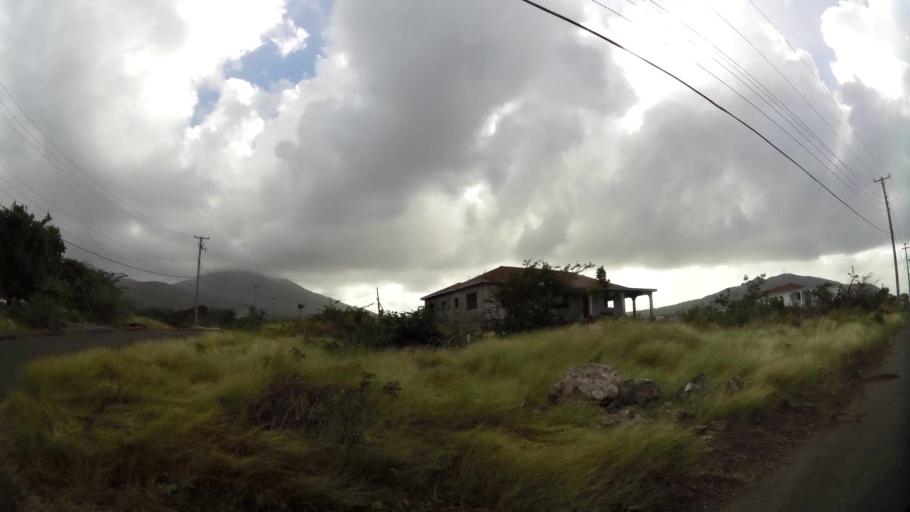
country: KN
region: Saint James Windwa
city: Newcastle
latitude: 17.2005
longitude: -62.5789
